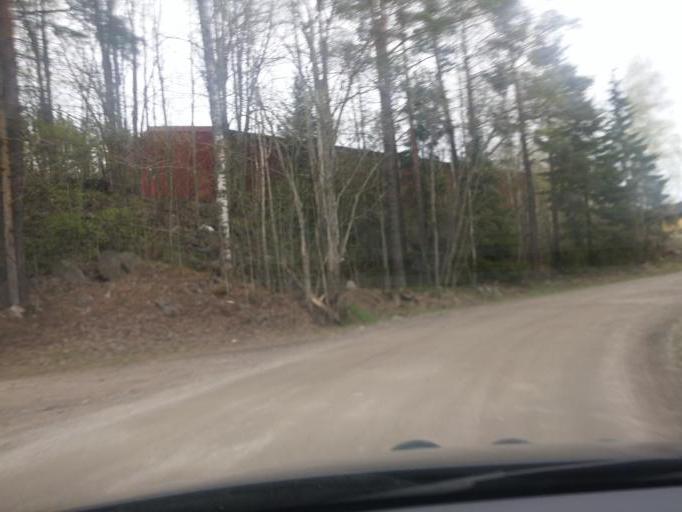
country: SE
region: Gaevleborg
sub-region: Ljusdals Kommun
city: Ljusdal
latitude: 61.8665
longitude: 16.0125
